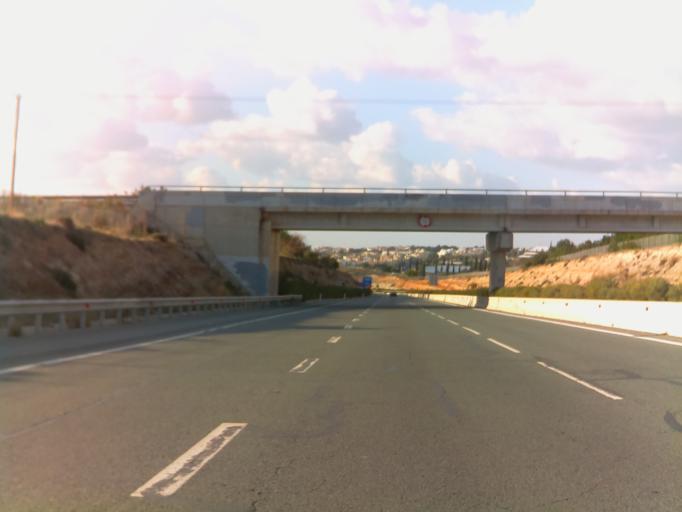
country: CY
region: Pafos
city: Paphos
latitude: 34.7784
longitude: 32.4563
